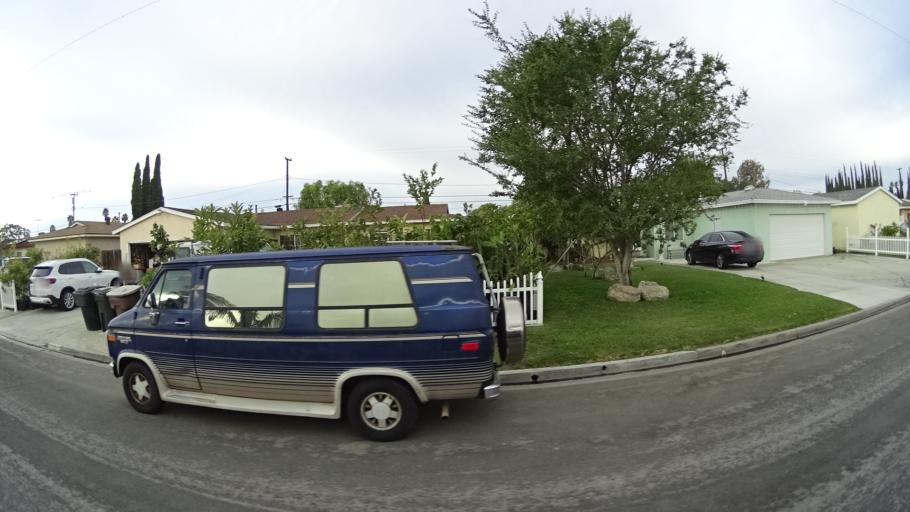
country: US
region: California
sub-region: Orange County
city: Garden Grove
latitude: 33.7710
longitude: -117.9234
